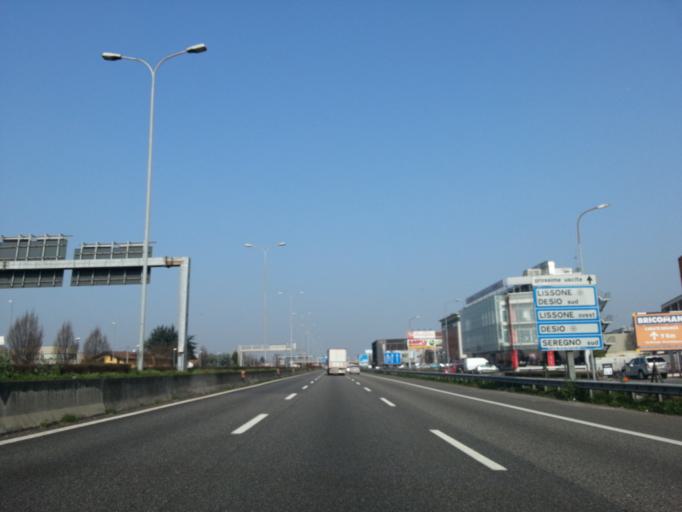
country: IT
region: Lombardy
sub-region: Provincia di Monza e Brianza
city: Lissone
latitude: 45.6019
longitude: 9.2315
